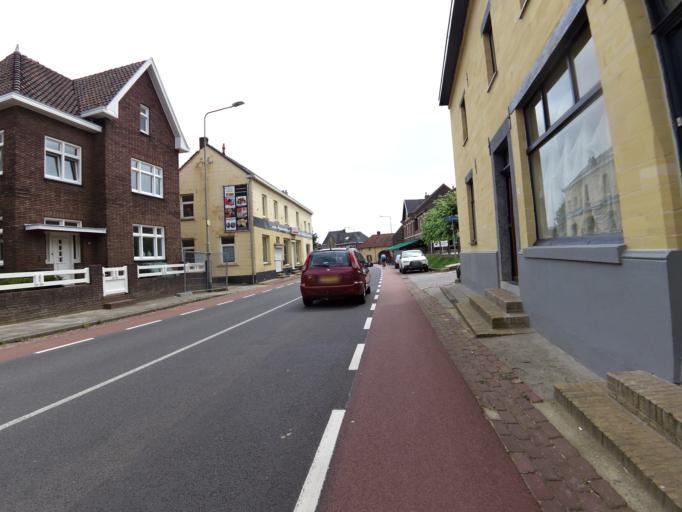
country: NL
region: Limburg
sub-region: Valkenburg aan de Geul
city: Schin op Geul
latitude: 50.8509
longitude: 5.8671
